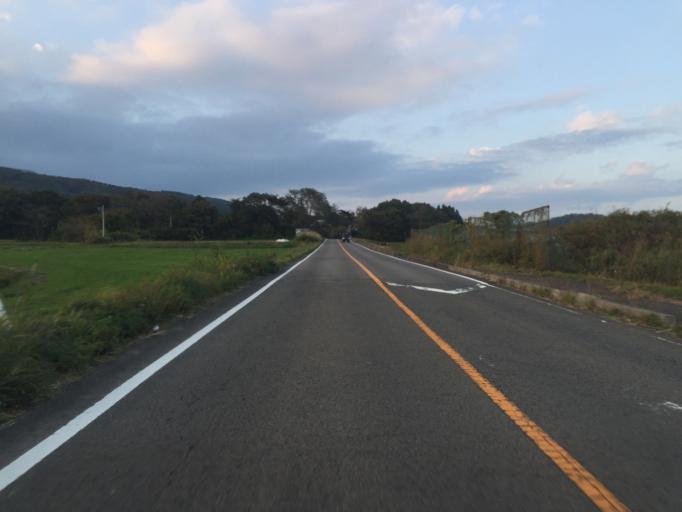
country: JP
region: Fukushima
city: Nihommatsu
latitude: 37.5913
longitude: 140.3560
